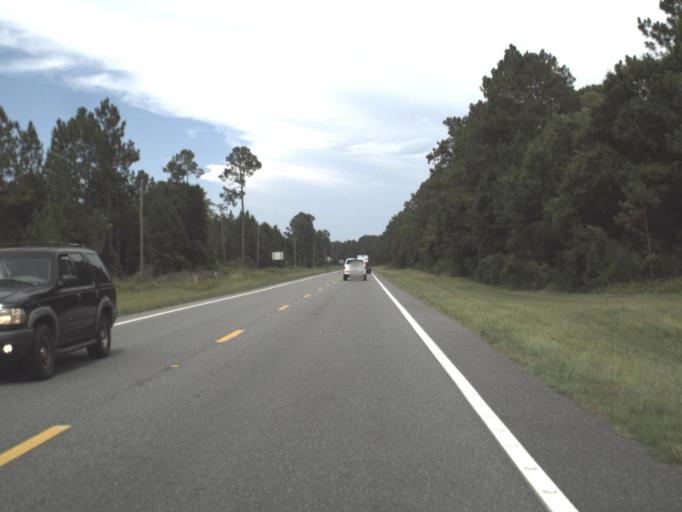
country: US
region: Florida
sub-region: Taylor County
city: Perry
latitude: 30.1005
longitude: -83.4525
